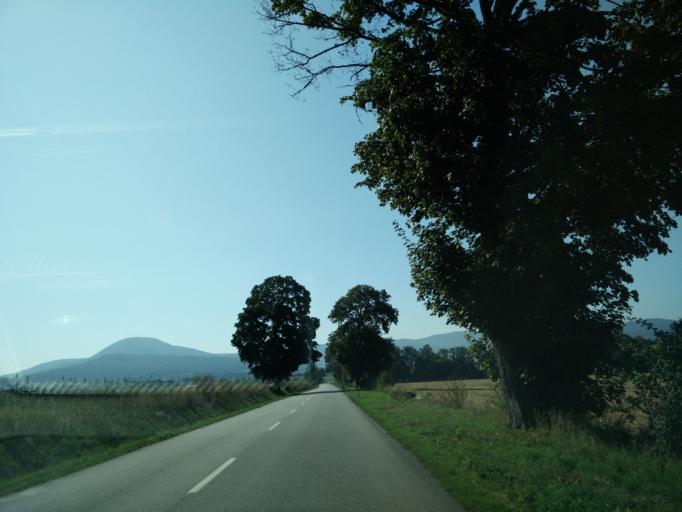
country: SK
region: Nitriansky
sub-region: Okres Nitra
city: Nitra
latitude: 48.4075
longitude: 18.1173
